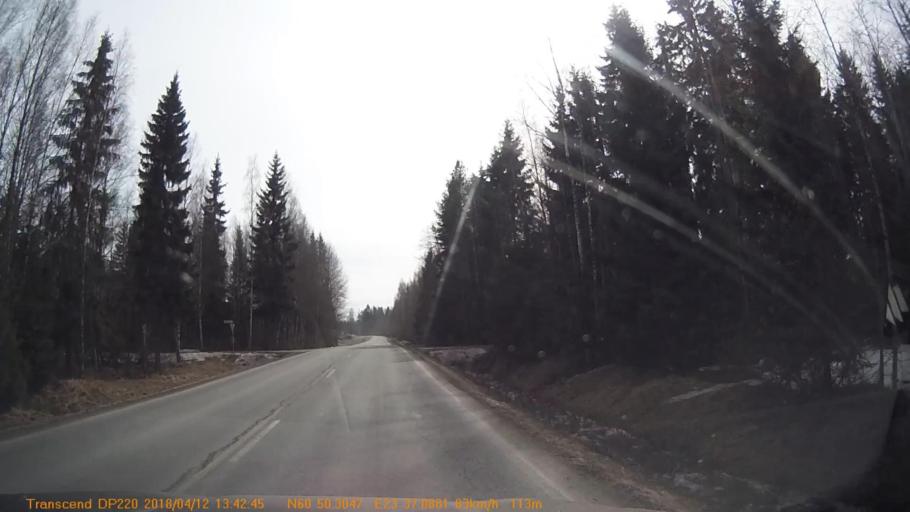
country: FI
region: Haeme
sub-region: Forssa
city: Forssa
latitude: 60.8377
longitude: 23.6182
